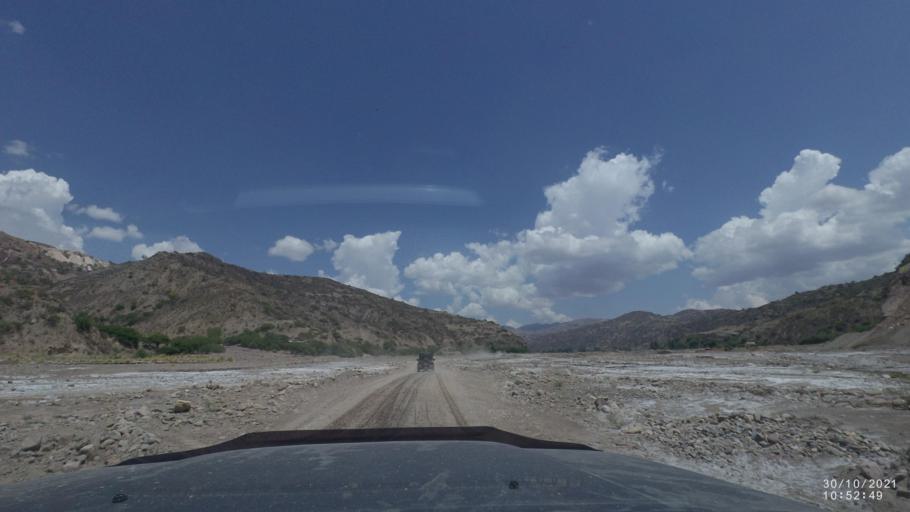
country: BO
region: Cochabamba
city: Sipe Sipe
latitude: -17.5510
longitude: -66.4800
